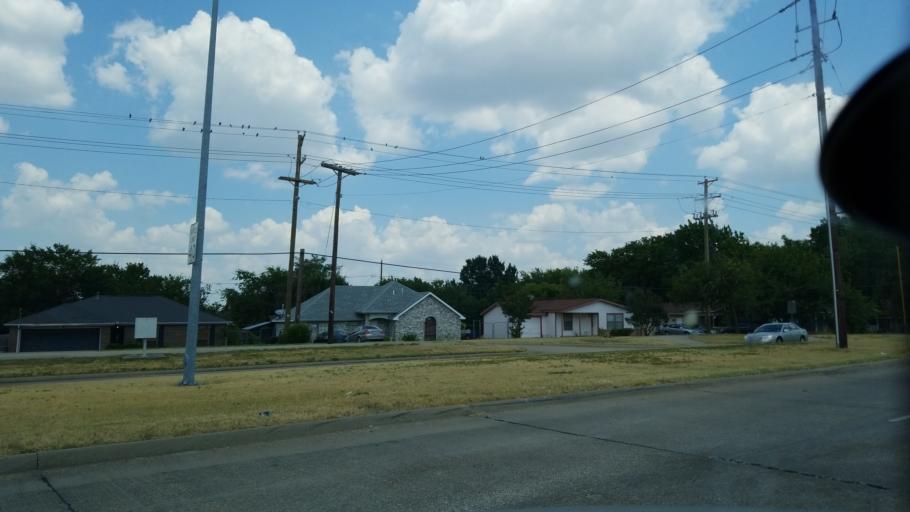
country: US
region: Texas
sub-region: Dallas County
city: Duncanville
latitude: 32.6762
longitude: -96.9032
